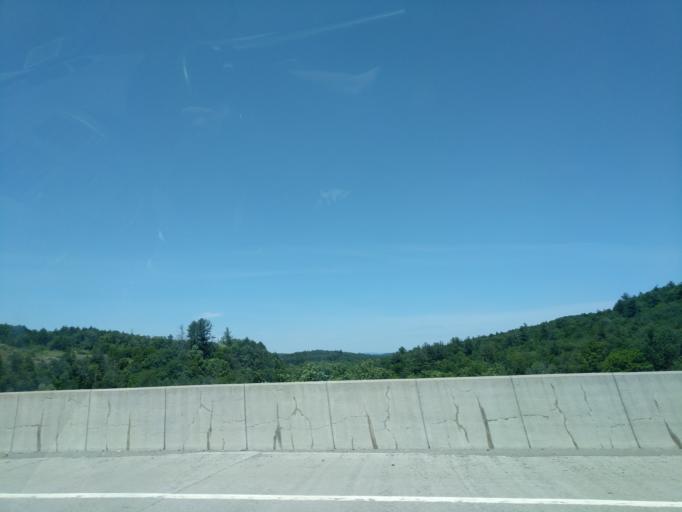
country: US
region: New York
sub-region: Sullivan County
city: Rock Hill
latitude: 41.6366
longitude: -74.6183
